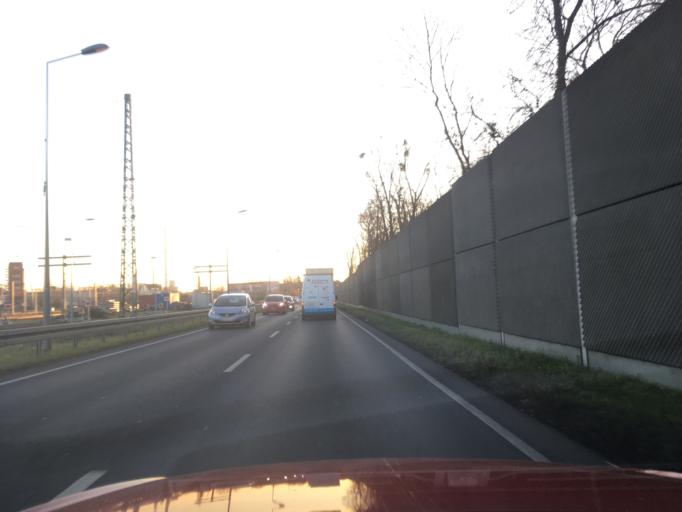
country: DE
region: Saxony-Anhalt
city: Dessau
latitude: 51.8379
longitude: 12.2321
